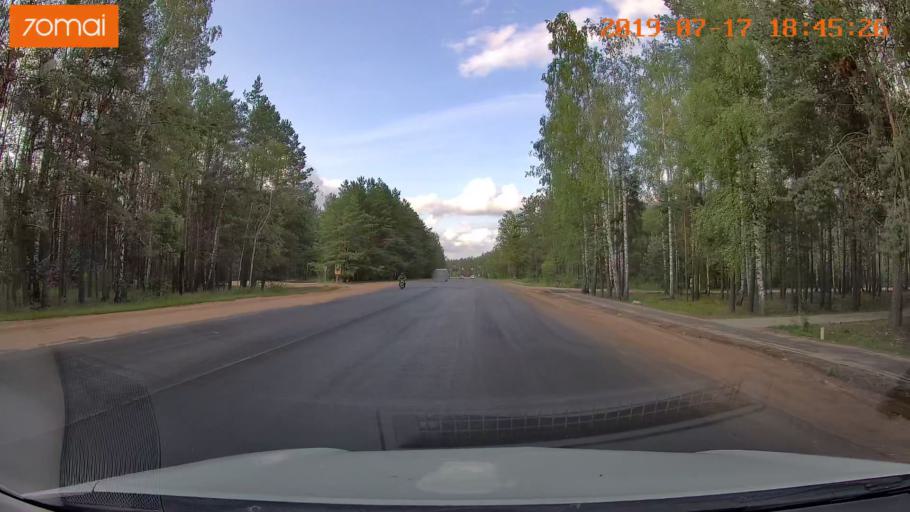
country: BY
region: Mogilev
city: Asipovichy
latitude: 53.3248
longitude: 28.6547
